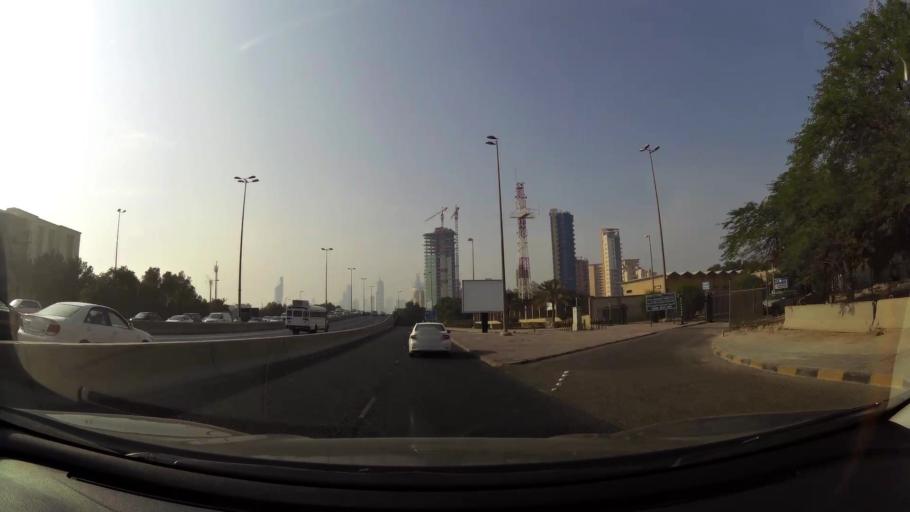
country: KW
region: Al Asimah
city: Ad Dasmah
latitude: 29.3645
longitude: 48.0135
